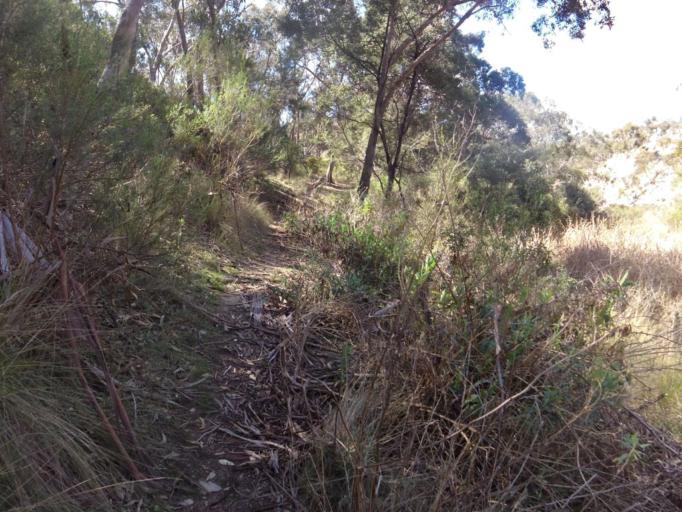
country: AU
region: Victoria
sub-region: Moorabool
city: Bacchus Marsh
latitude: -37.6582
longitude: 144.4979
